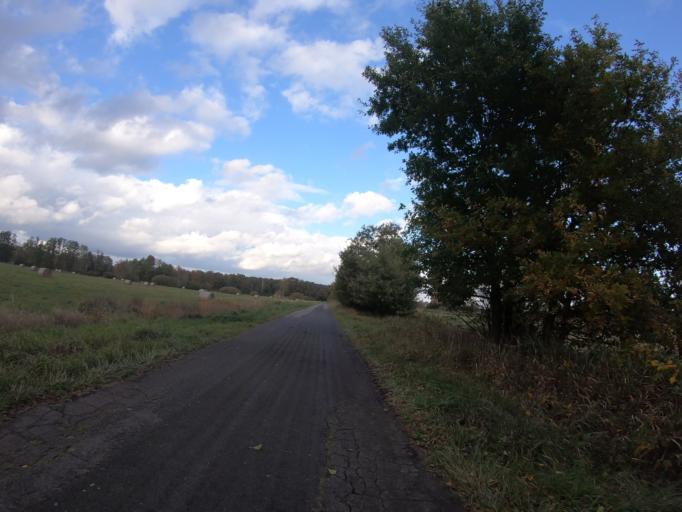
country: DE
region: Lower Saxony
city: Wagenhoff
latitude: 52.5441
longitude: 10.5578
